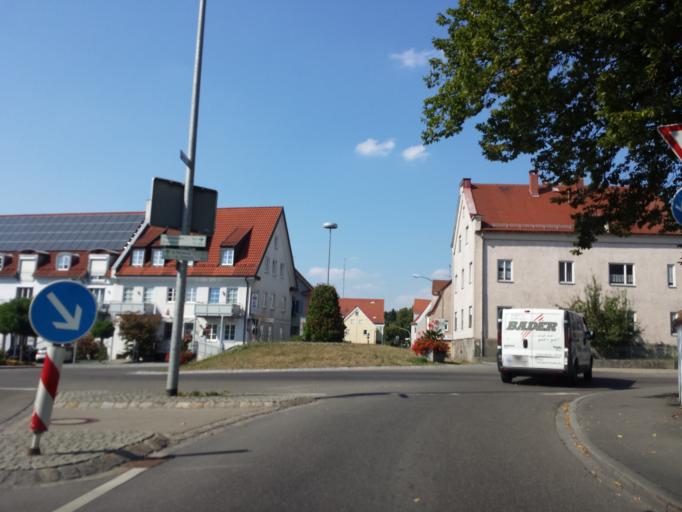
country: DE
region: Bavaria
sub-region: Swabia
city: Krumbach
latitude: 48.2437
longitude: 10.3706
